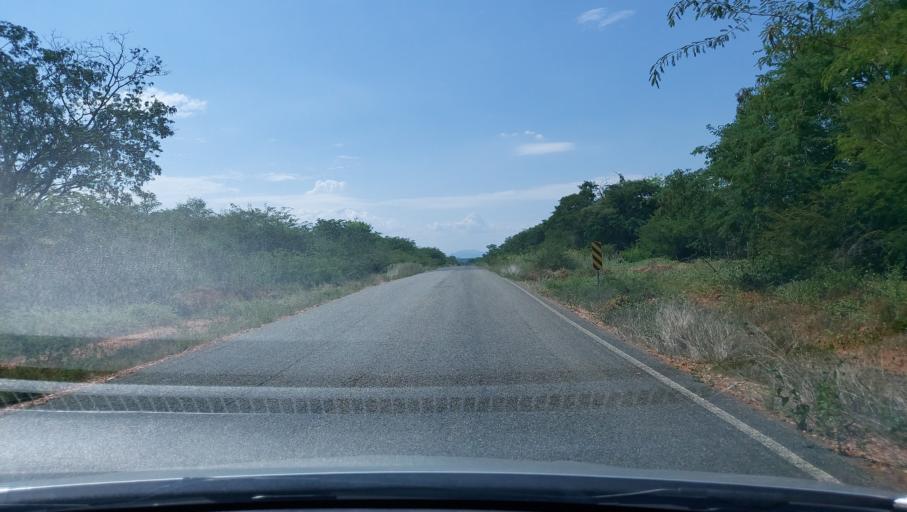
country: BR
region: Bahia
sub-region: Oliveira Dos Brejinhos
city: Beira Rio
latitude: -12.1796
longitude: -42.5424
